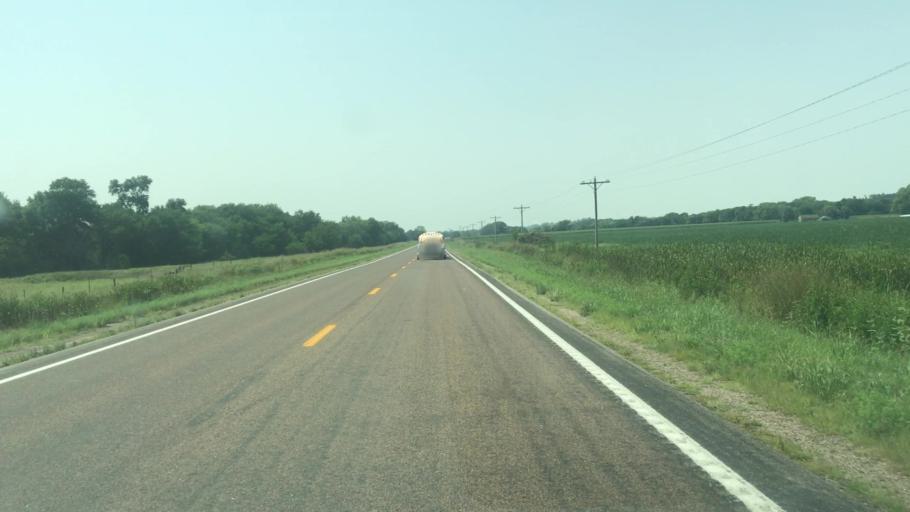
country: US
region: Nebraska
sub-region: Buffalo County
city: Ravenna
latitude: 41.0760
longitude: -98.6735
